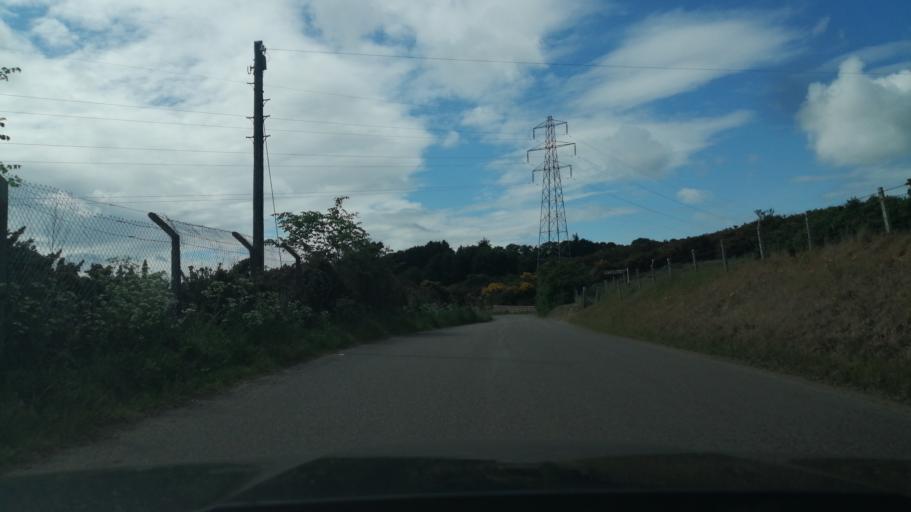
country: GB
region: Scotland
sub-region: Moray
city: Elgin
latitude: 57.6541
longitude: -3.2913
